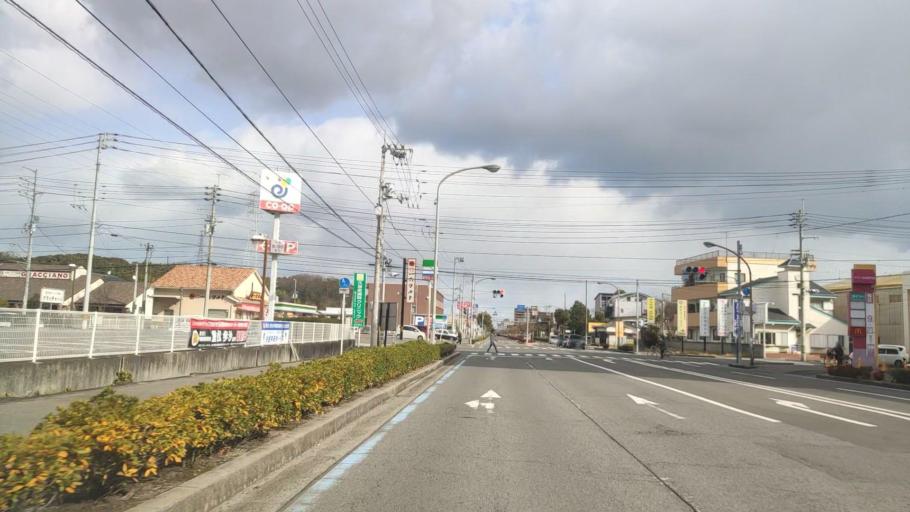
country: JP
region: Ehime
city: Hojo
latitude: 34.0566
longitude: 132.9794
